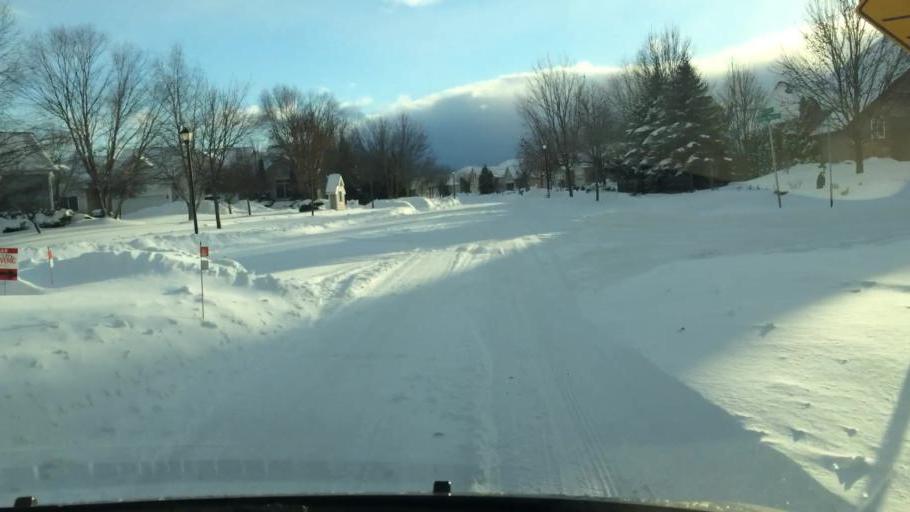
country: US
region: Ohio
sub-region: Portage County
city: Kent
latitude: 41.1626
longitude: -81.3777
